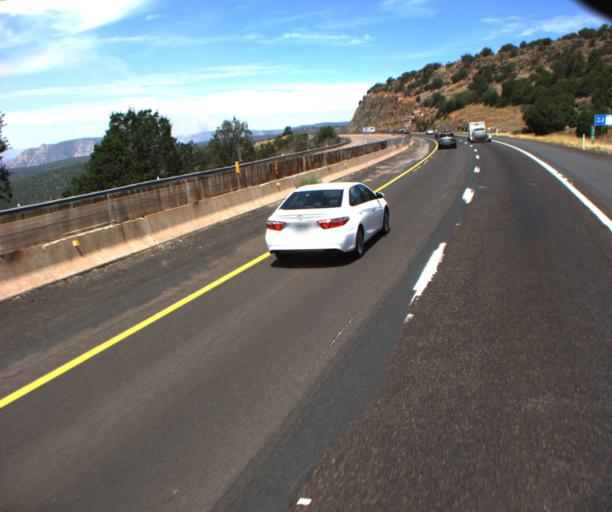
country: US
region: Arizona
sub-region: Yavapai County
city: Village of Oak Creek (Big Park)
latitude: 34.8075
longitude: -111.5998
